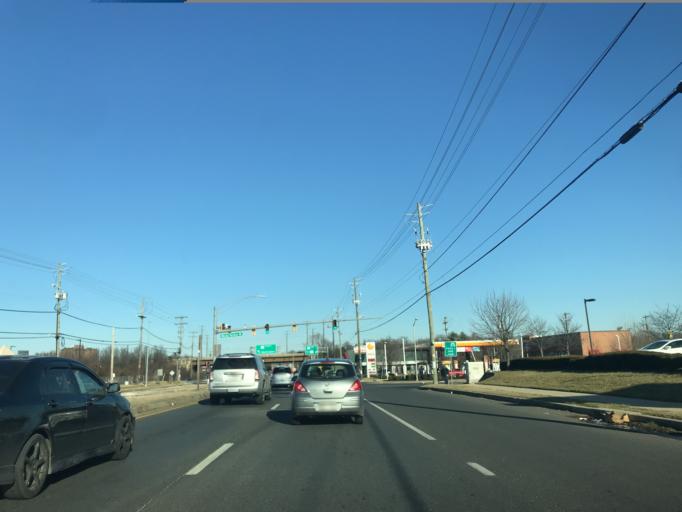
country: US
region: Maryland
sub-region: Prince George's County
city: Clinton
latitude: 38.7670
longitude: -76.8879
